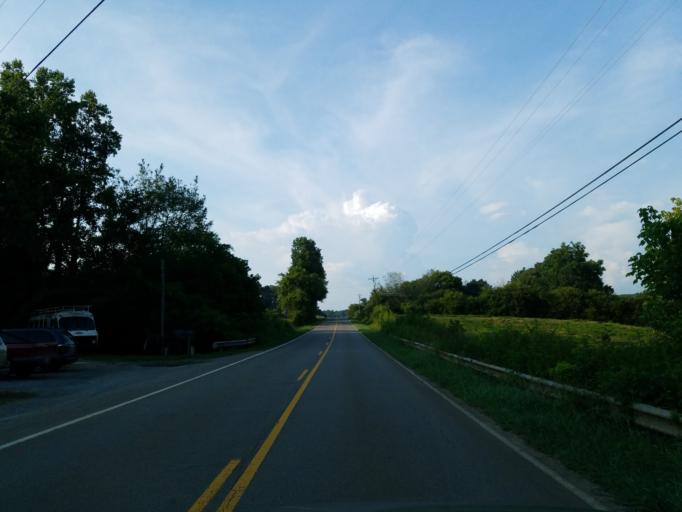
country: US
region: Georgia
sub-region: Gilmer County
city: Ellijay
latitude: 34.5644
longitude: -84.5376
